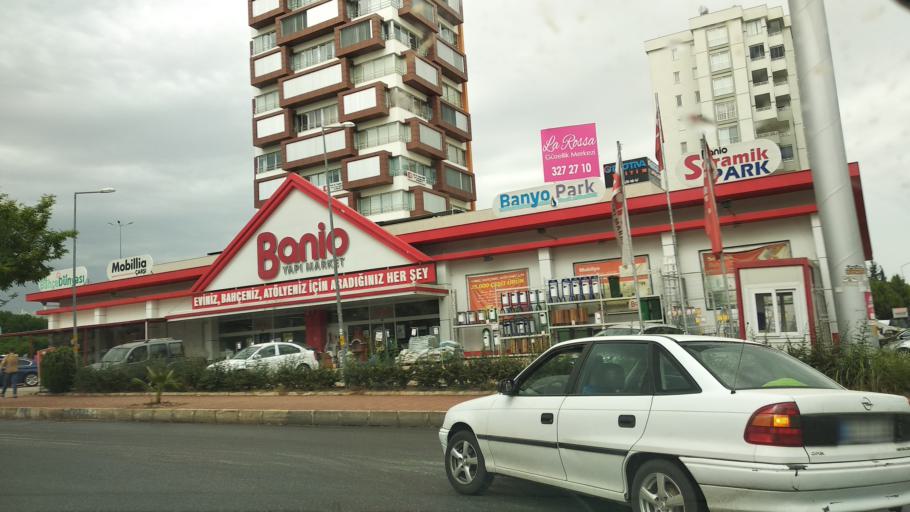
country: TR
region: Mersin
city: Mercin
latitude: 36.7984
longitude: 34.5952
